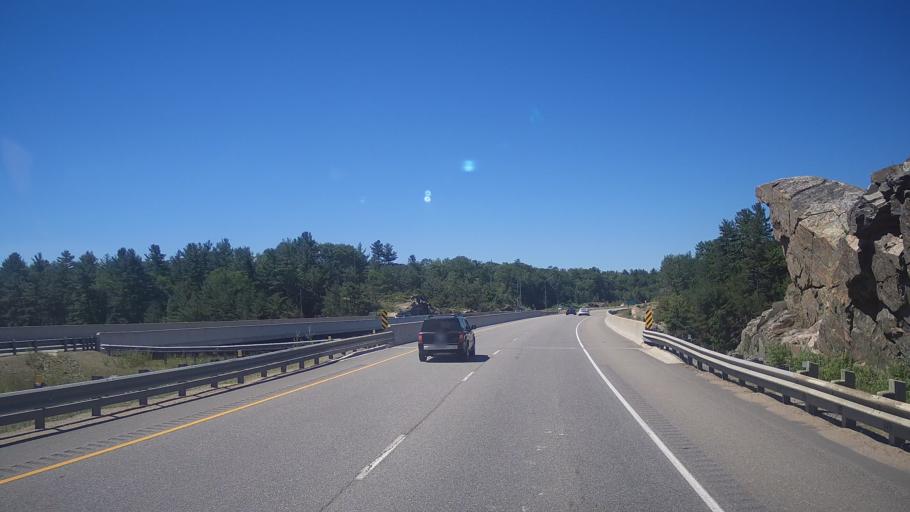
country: CA
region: Ontario
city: Gravenhurst
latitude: 44.9124
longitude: -79.3461
